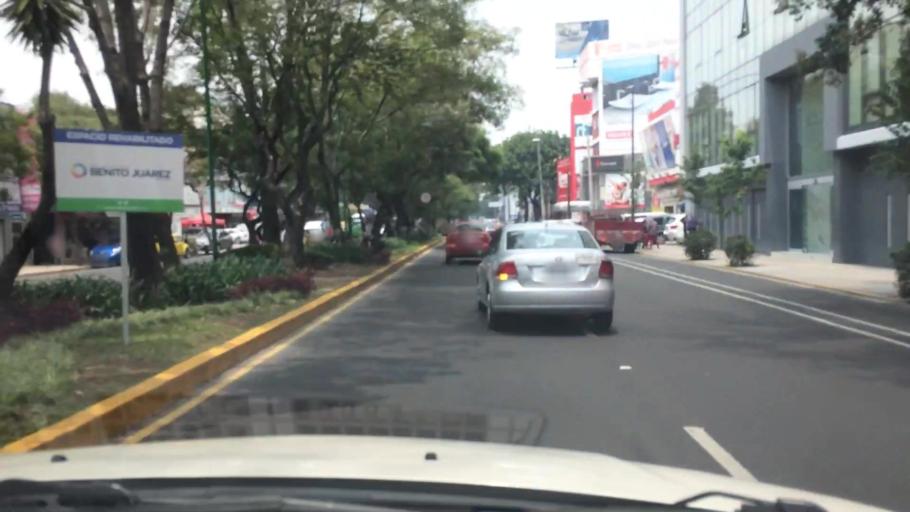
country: MX
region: Mexico City
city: Coyoacan
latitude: 19.3639
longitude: -99.1548
